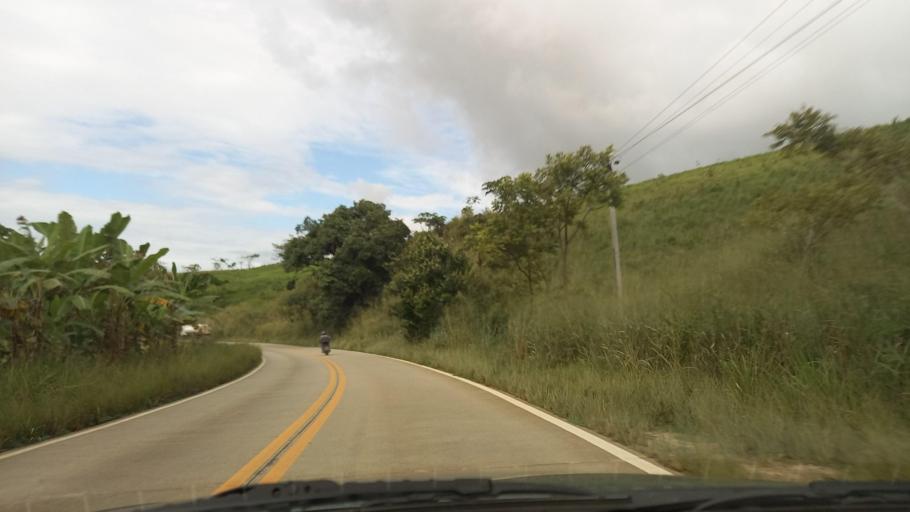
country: BR
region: Pernambuco
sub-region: Maraial
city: Maraial
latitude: -8.7553
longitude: -35.8435
